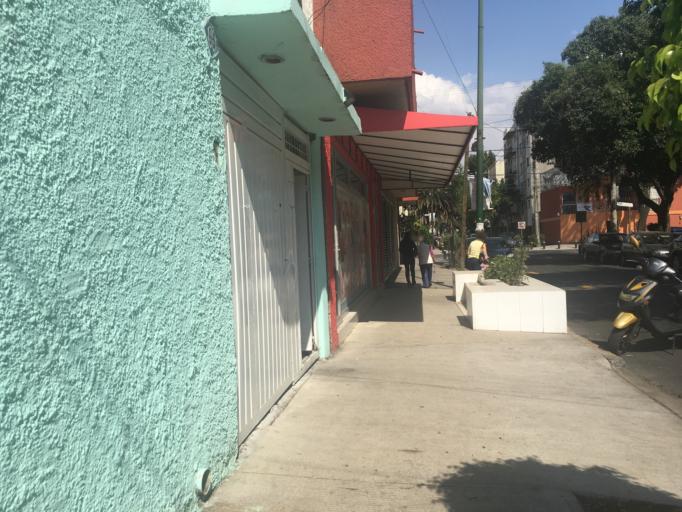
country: MX
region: Mexico City
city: Coyoacan
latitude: 19.3596
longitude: -99.1473
